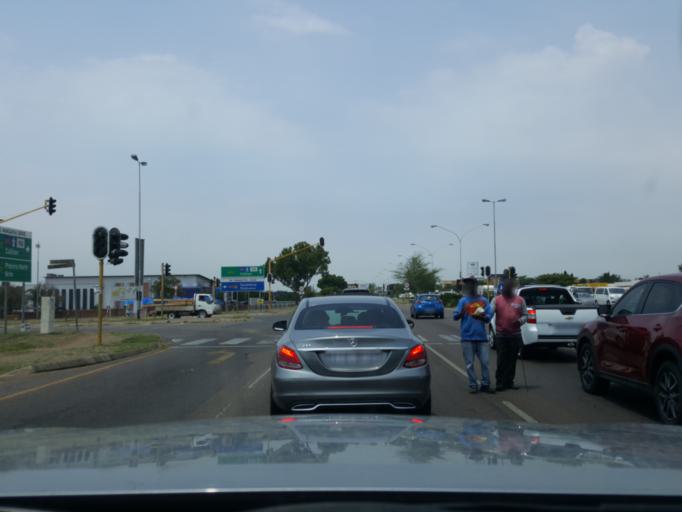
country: ZA
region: Gauteng
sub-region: City of Tshwane Metropolitan Municipality
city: Pretoria
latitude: -25.6787
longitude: 28.2423
